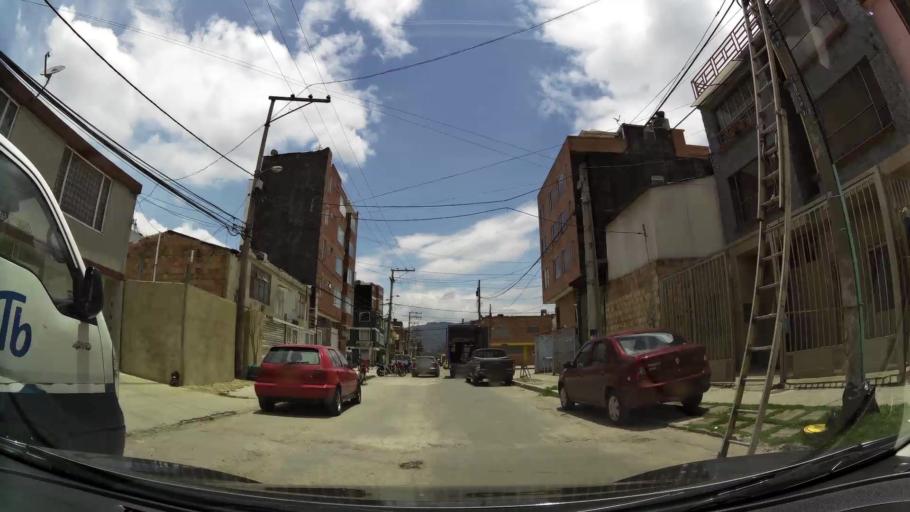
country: CO
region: Bogota D.C.
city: Barrio San Luis
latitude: 4.7133
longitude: -74.0629
